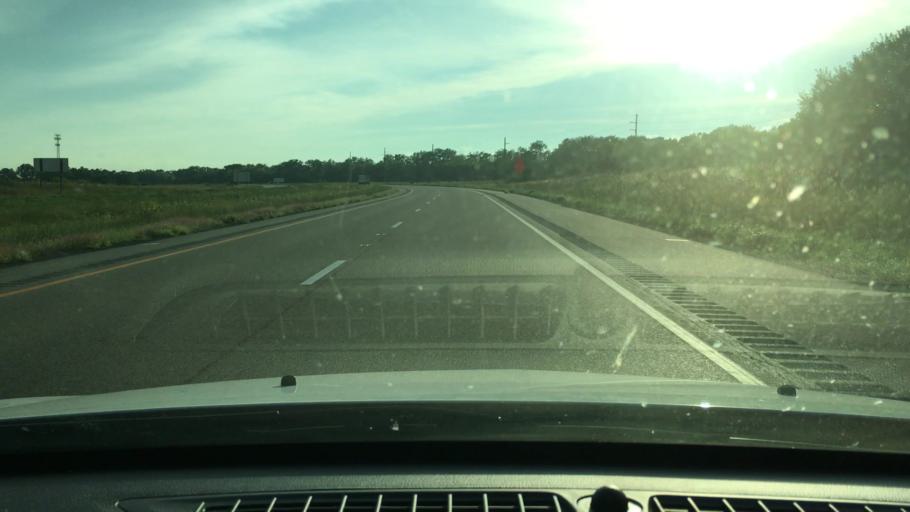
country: US
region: Illinois
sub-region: Logan County
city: Atlanta
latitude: 40.2507
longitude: -89.2394
